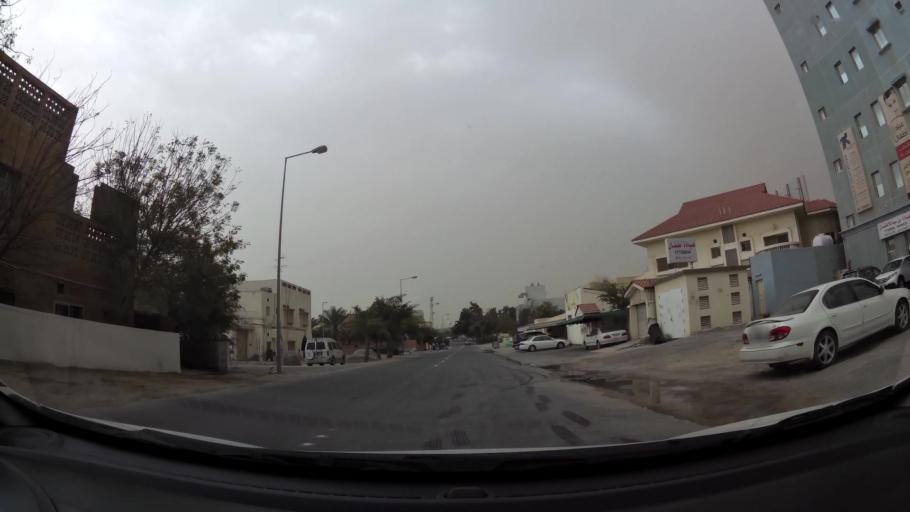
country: BH
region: Northern
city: Madinat `Isa
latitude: 26.1714
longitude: 50.5435
